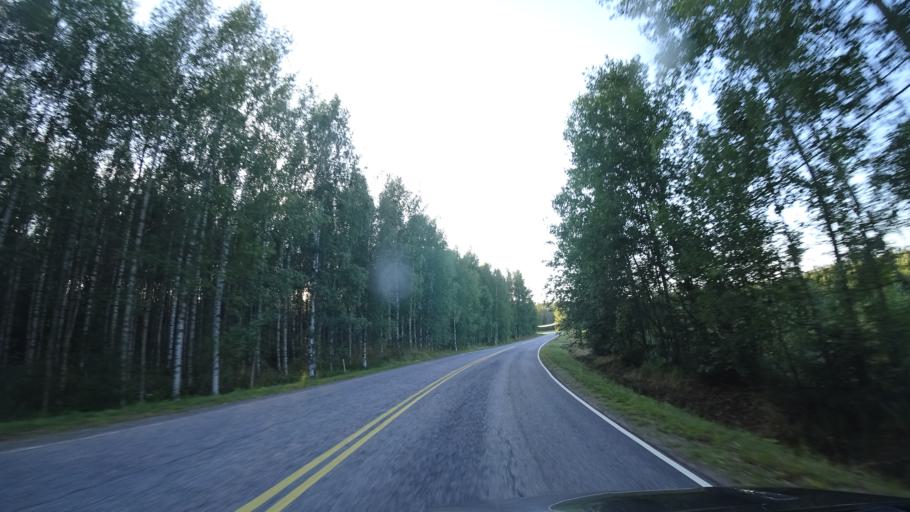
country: FI
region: Haeme
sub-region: Haemeenlinna
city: Tuulos
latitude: 61.0073
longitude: 24.8644
